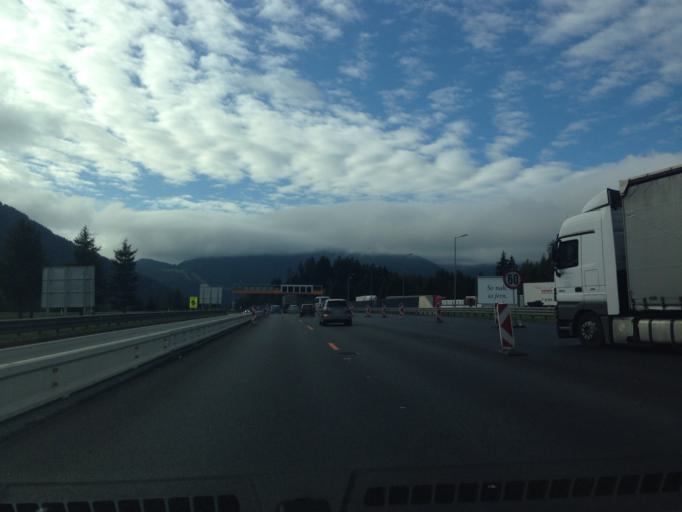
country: AT
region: Tyrol
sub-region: Politischer Bezirk Innsbruck Land
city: Gries am Brenner
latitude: 47.0595
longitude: 11.4799
